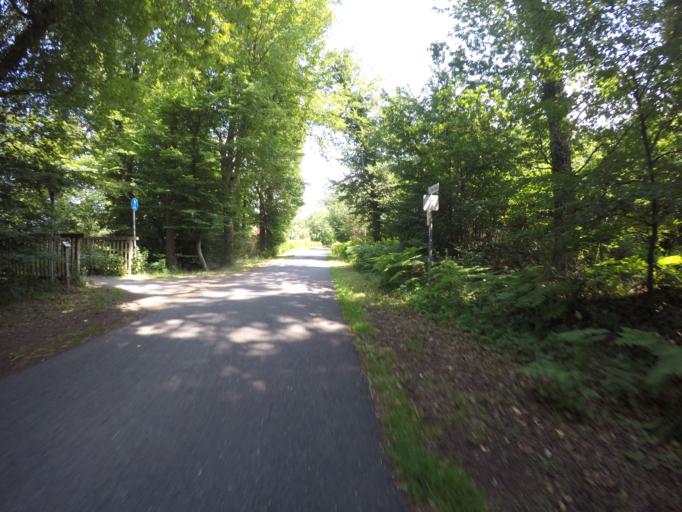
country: DE
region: North Rhine-Westphalia
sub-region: Regierungsbezirk Munster
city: Rhede
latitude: 51.8233
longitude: 6.7512
